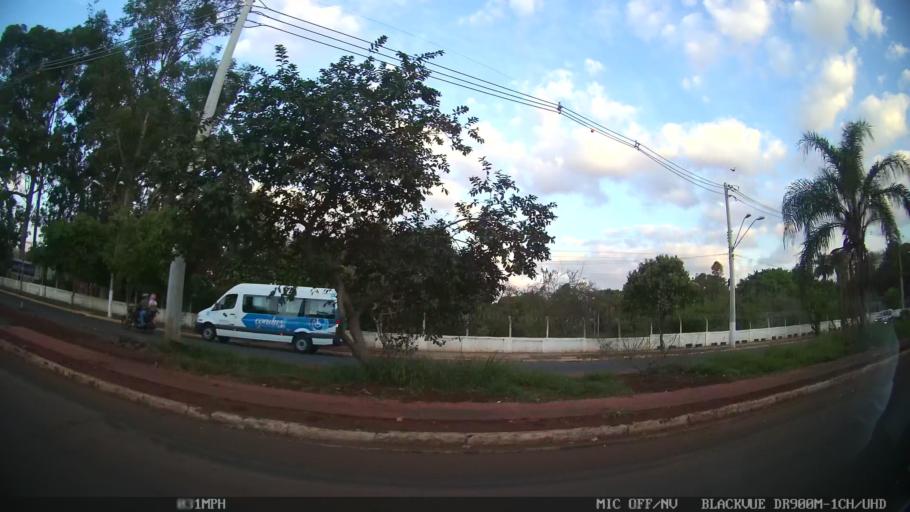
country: BR
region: Sao Paulo
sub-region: Ribeirao Preto
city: Ribeirao Preto
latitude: -21.1537
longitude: -47.7820
